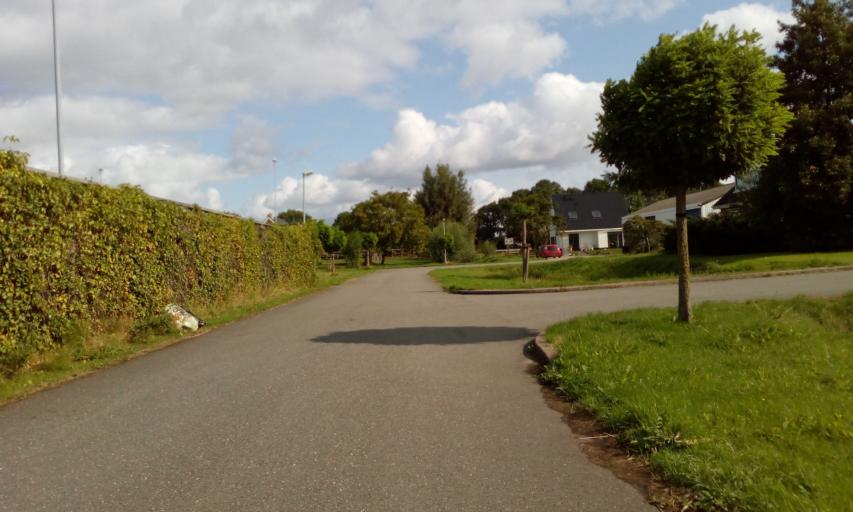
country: NL
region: South Holland
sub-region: Gemeente Lansingerland
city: Bleiswijk
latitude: 52.0003
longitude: 4.5319
